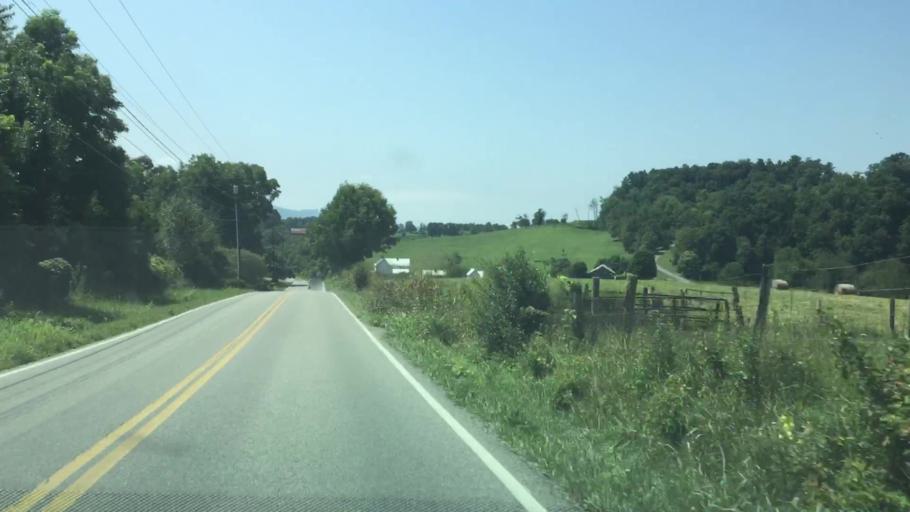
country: US
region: Tennessee
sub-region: Sullivan County
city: Fairmount
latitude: 36.5938
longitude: -82.0473
